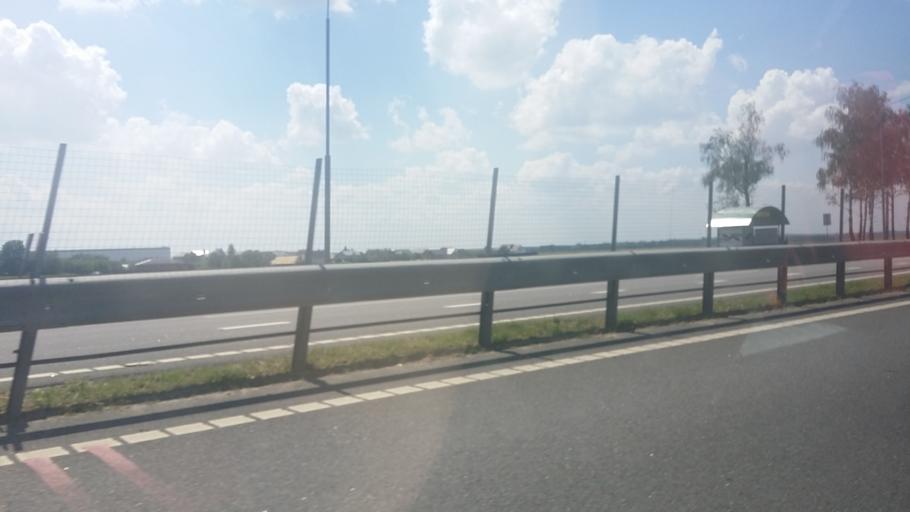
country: BY
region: Minsk
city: Luhavaya Slabada
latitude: 53.7617
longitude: 27.9124
